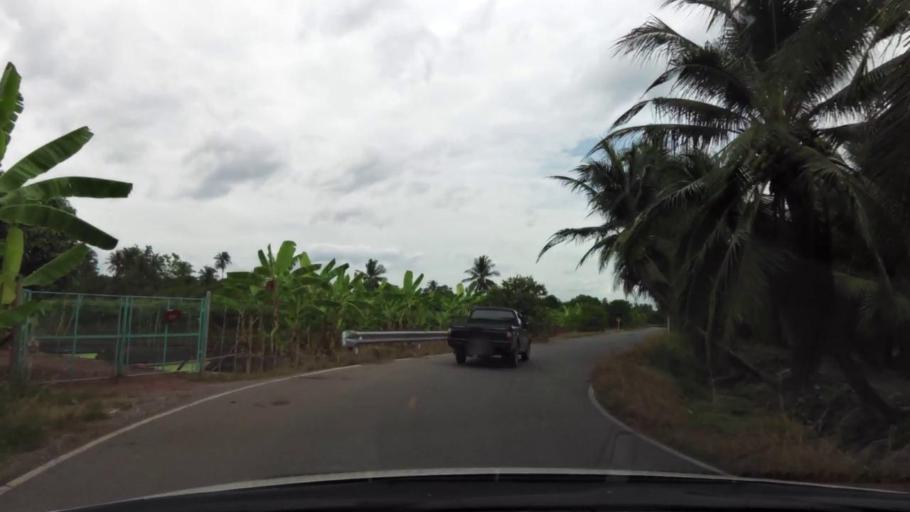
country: TH
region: Samut Sakhon
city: Ban Phaeo
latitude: 13.5621
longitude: 100.0408
